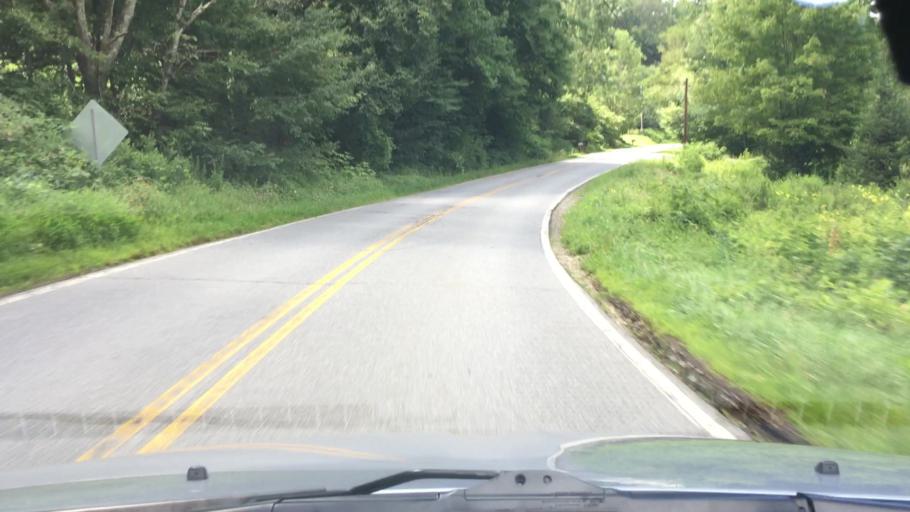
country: US
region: North Carolina
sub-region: Madison County
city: Mars Hill
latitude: 35.9414
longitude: -82.5272
